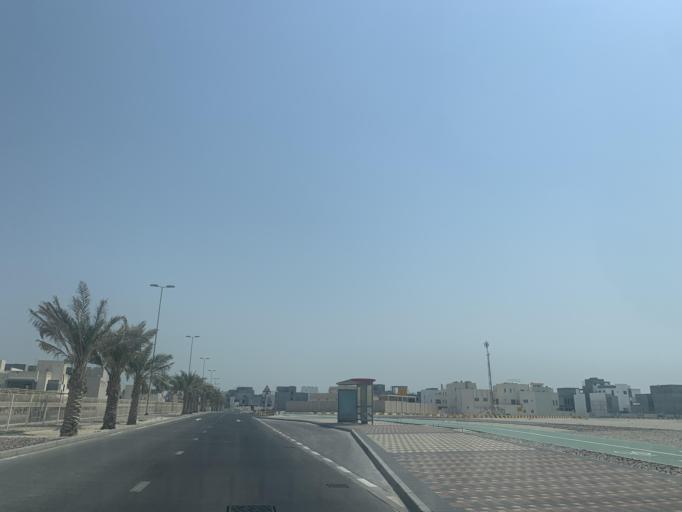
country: BH
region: Muharraq
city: Al Hadd
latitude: 26.2429
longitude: 50.6633
